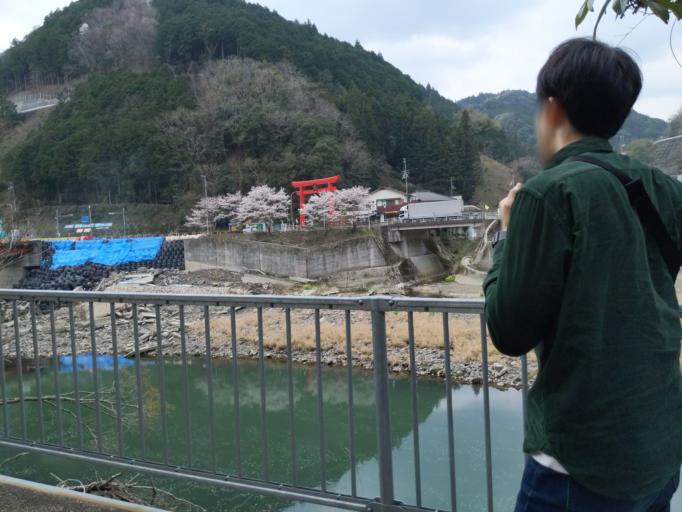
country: JP
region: Ehime
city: Ozu
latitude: 33.4560
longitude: 132.6805
